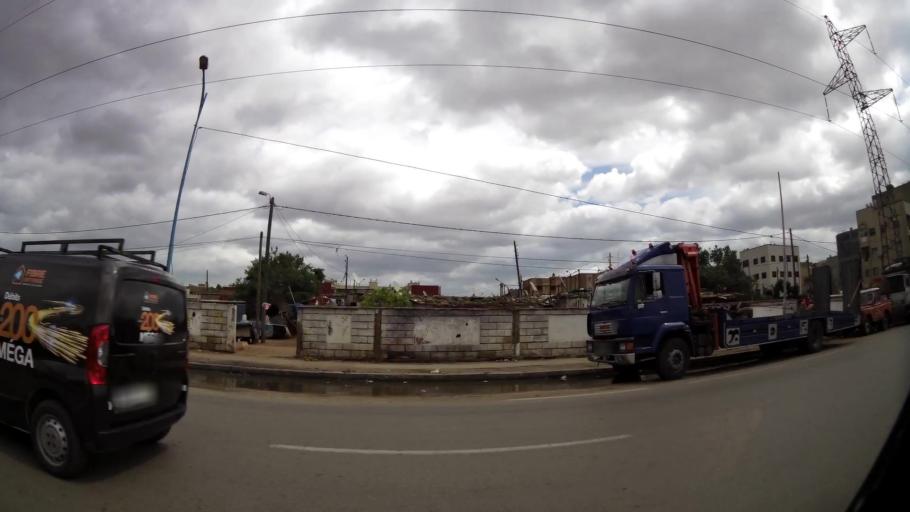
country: MA
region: Grand Casablanca
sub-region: Mediouna
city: Tit Mellil
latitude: 33.5824
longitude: -7.5444
